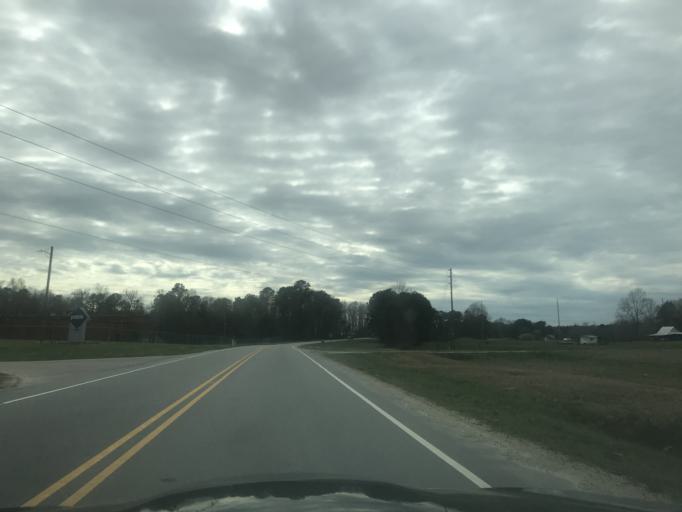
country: US
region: North Carolina
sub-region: Franklin County
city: Louisburg
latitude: 36.0838
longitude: -78.3353
